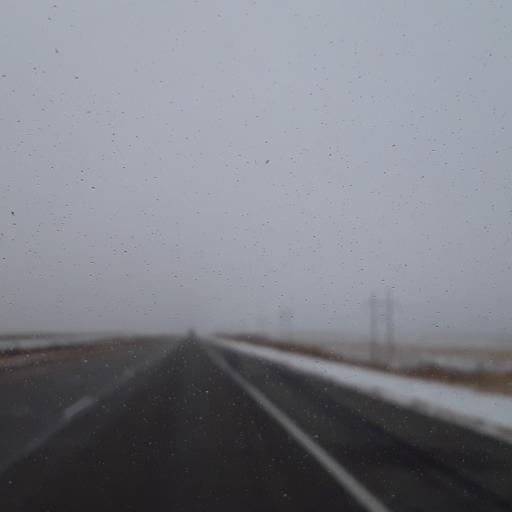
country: US
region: Nebraska
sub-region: Cheyenne County
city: Sidney
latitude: 40.8059
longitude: -102.8544
